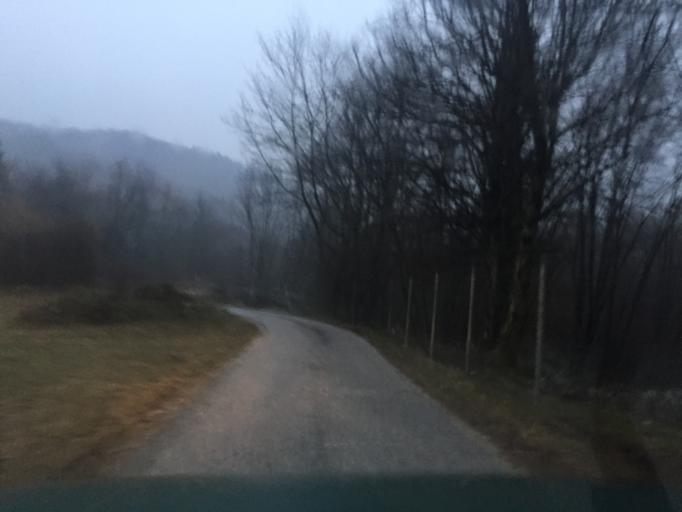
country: SI
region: Kanal
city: Kanal
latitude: 46.0510
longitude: 13.6663
